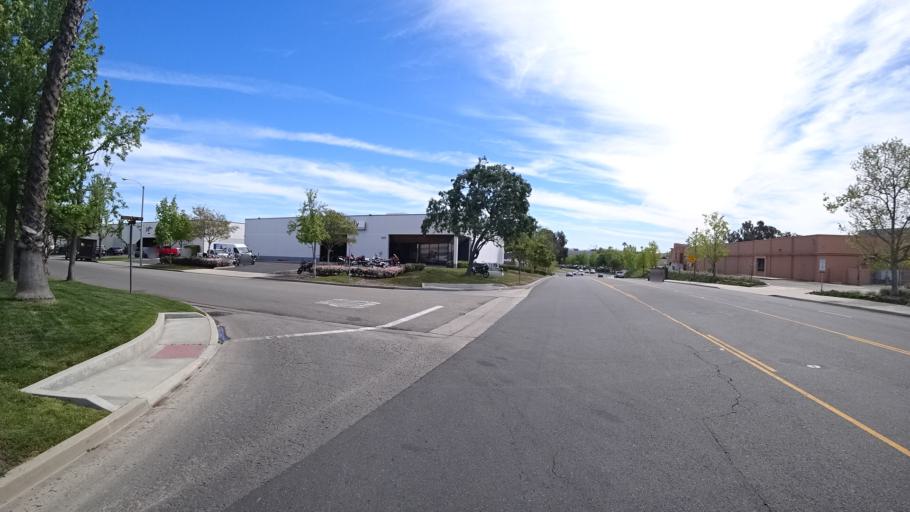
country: US
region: California
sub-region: Ventura County
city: Casa Conejo
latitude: 34.1900
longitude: -118.9317
